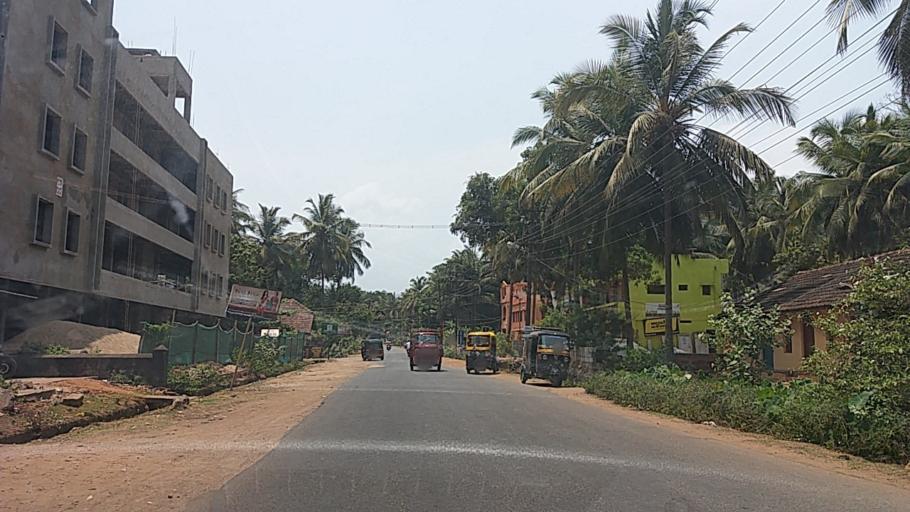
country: IN
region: Karnataka
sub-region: Uttar Kannada
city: Karwar
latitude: 14.8115
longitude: 74.1443
